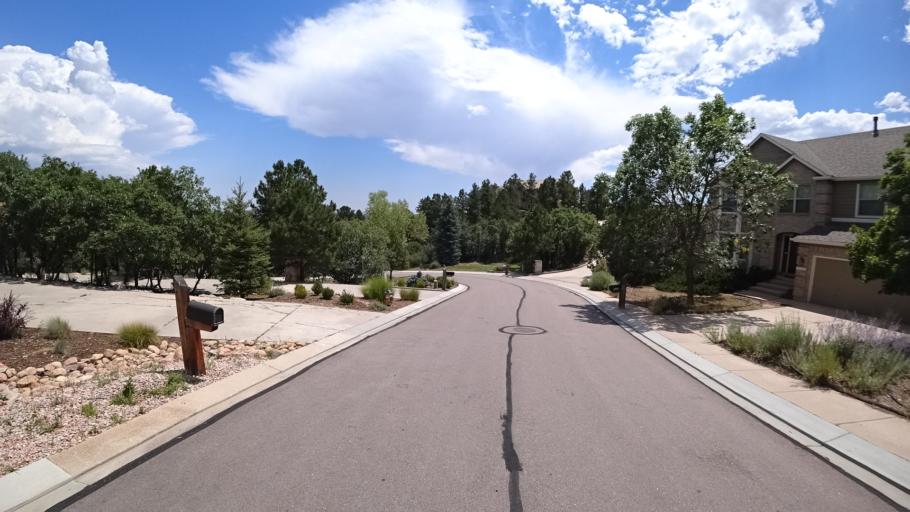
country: US
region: Colorado
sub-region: El Paso County
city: Air Force Academy
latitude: 38.9385
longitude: -104.8447
